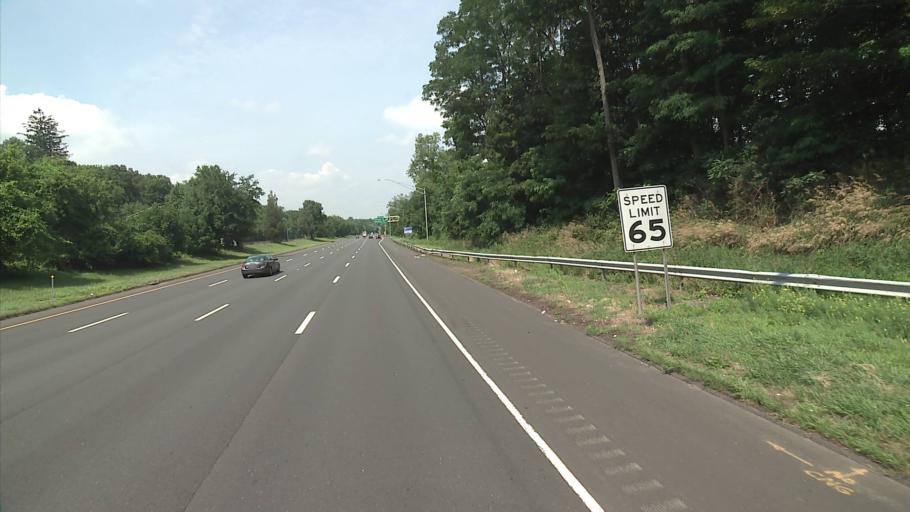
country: US
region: Connecticut
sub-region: Hartford County
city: Manchester
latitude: 41.7631
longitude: -72.5321
